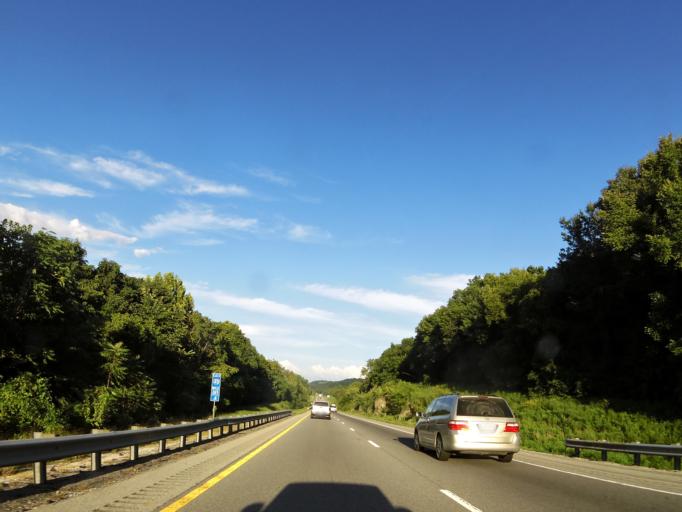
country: US
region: Tennessee
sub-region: Smith County
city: Gordonsville
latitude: 36.1404
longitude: -85.8358
